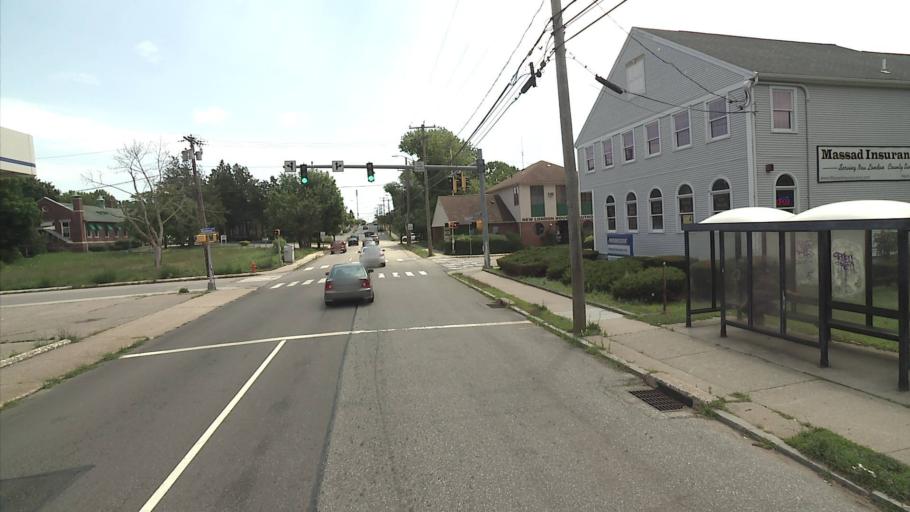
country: US
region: Connecticut
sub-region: New London County
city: New London
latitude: 41.3534
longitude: -72.1136
